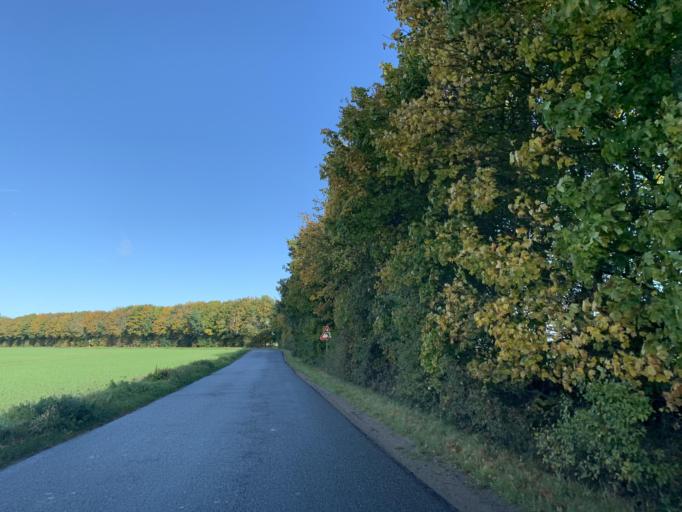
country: DE
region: Mecklenburg-Vorpommern
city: Gross Nemerow
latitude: 53.4714
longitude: 13.2694
